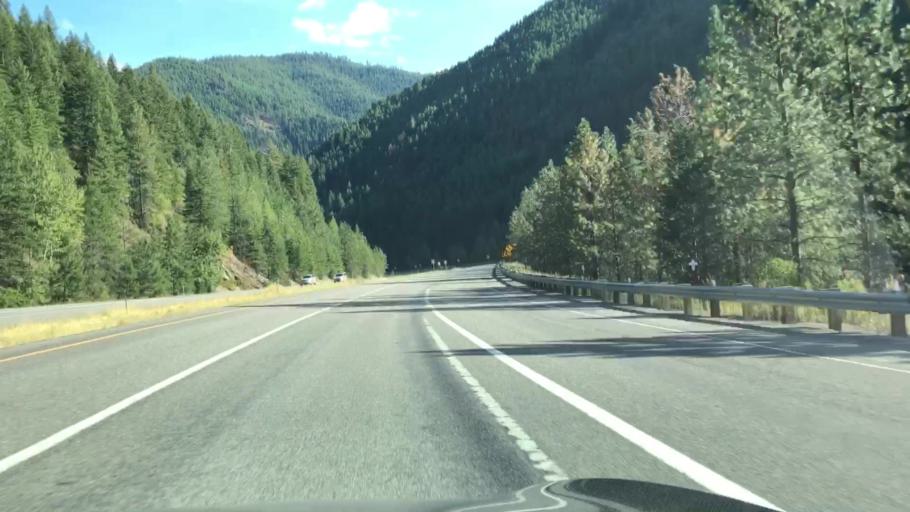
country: US
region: Montana
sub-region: Sanders County
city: Thompson Falls
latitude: 47.3198
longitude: -115.2452
